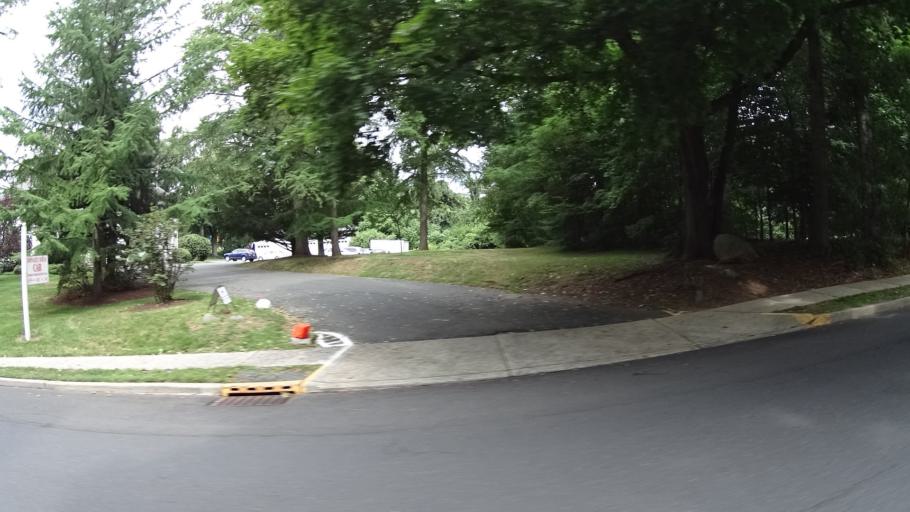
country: US
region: New Jersey
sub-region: Union County
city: New Providence
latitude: 40.7125
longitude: -74.3760
